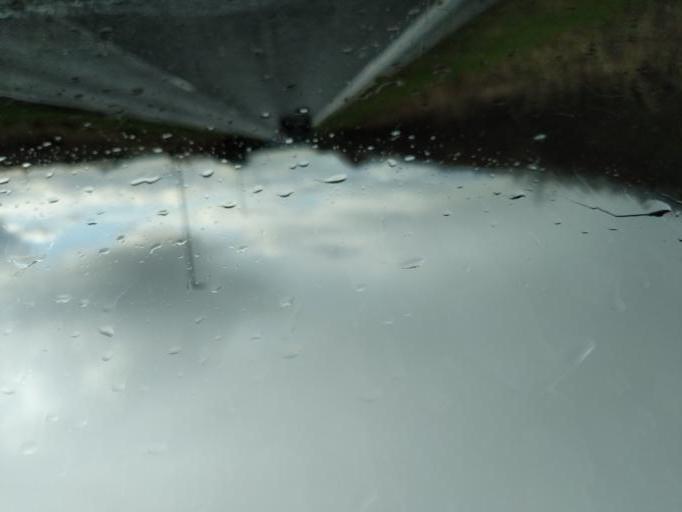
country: GB
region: England
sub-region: Northumberland
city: Seaton Delaval
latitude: 55.1028
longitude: -1.5354
